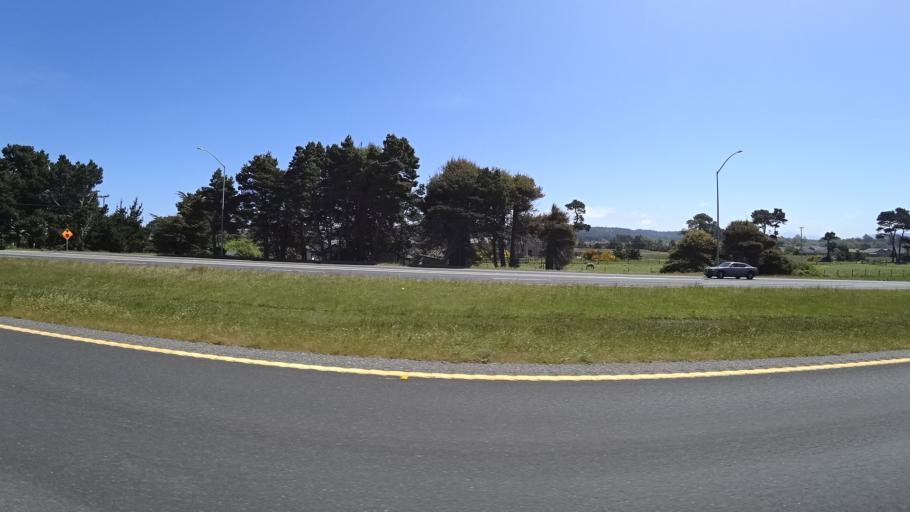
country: US
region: California
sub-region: Humboldt County
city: McKinleyville
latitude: 40.9668
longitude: -124.1162
